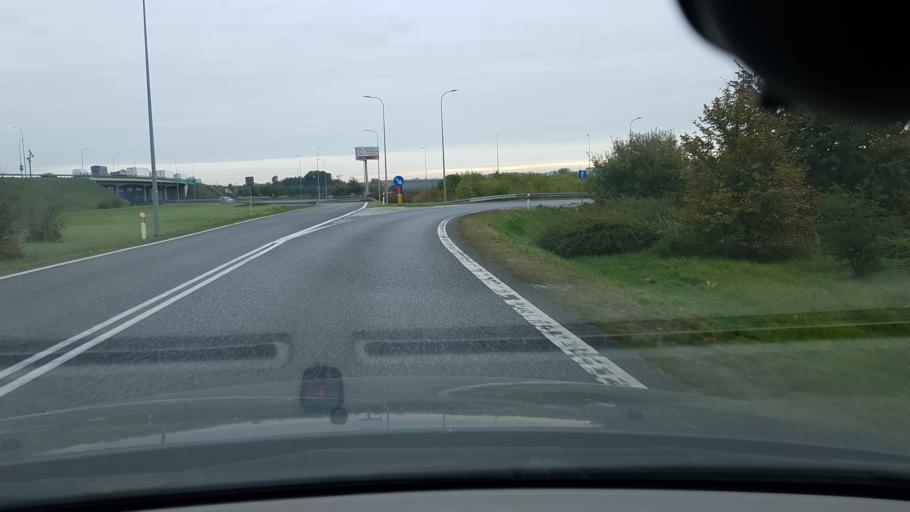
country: PL
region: Masovian Voivodeship
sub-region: Powiat zyrardowski
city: Mszczonow
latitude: 51.9827
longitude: 20.5179
